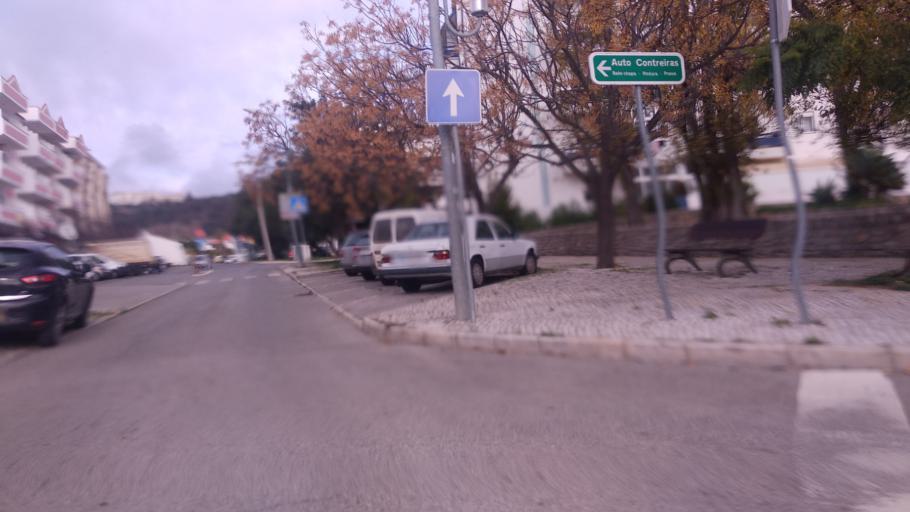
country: PT
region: Faro
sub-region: Sao Bras de Alportel
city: Sao Bras de Alportel
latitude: 37.1553
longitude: -7.8912
